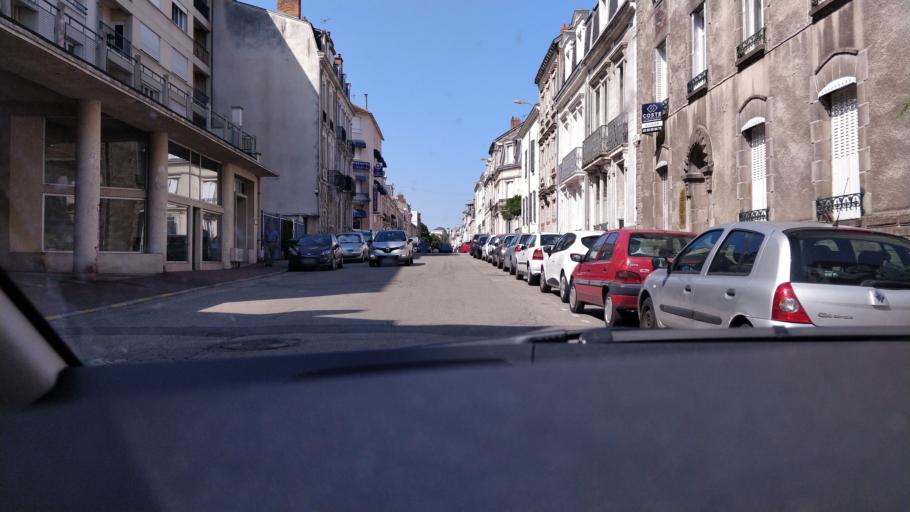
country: FR
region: Limousin
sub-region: Departement de la Haute-Vienne
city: Limoges
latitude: 45.8368
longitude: 1.2622
